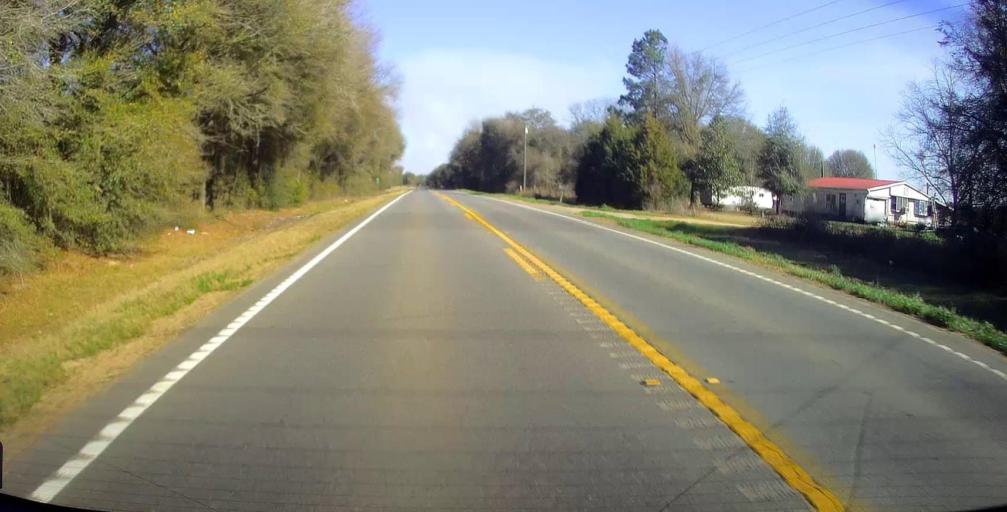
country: US
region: Georgia
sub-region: Macon County
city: Oglethorpe
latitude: 32.3324
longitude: -84.1036
